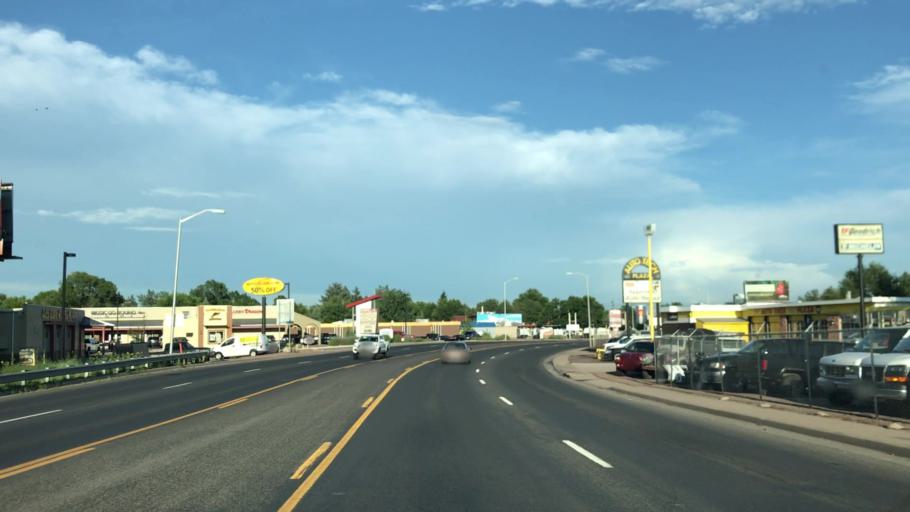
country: US
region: Colorado
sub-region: El Paso County
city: Colorado Springs
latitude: 38.8761
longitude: -104.8302
